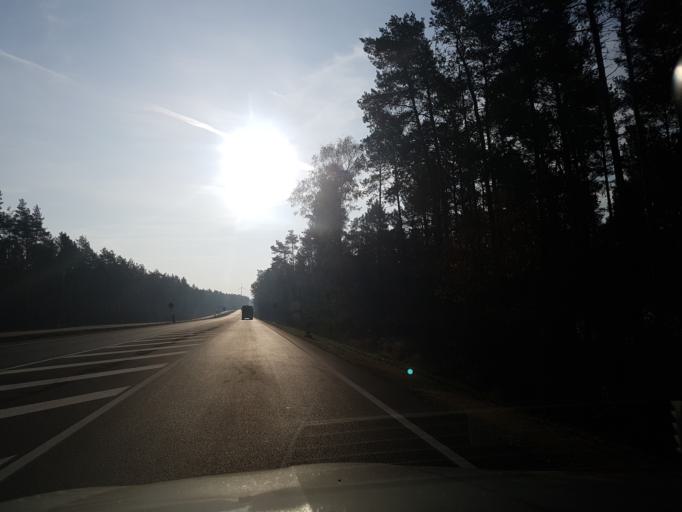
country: DE
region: Brandenburg
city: Elsterwerda
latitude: 51.4992
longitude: 13.4683
